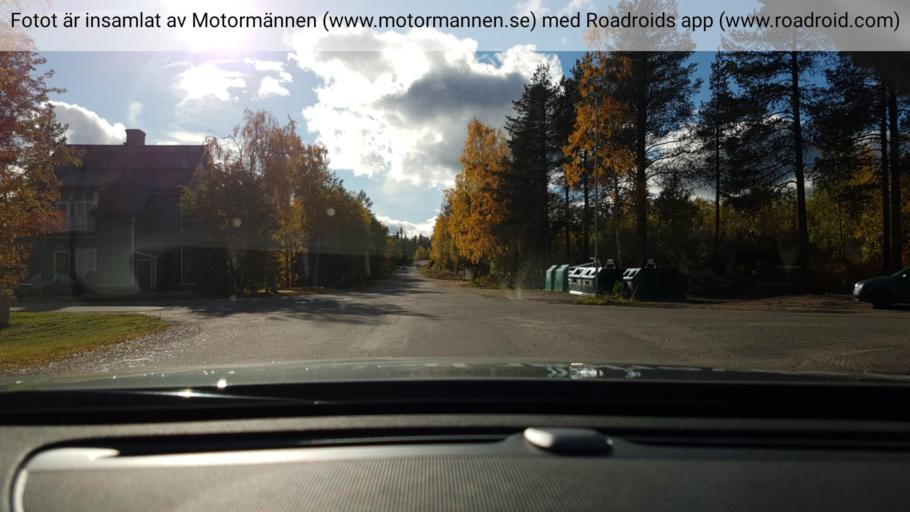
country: SE
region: Norrbotten
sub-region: Gallivare Kommun
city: Malmberget
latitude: 67.1825
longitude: 20.7304
